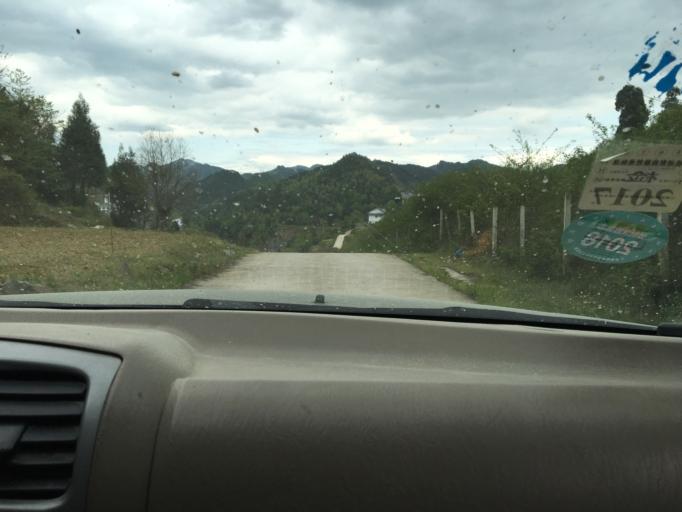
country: CN
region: Guizhou Sheng
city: Donghua
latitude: 28.0526
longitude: 108.0702
